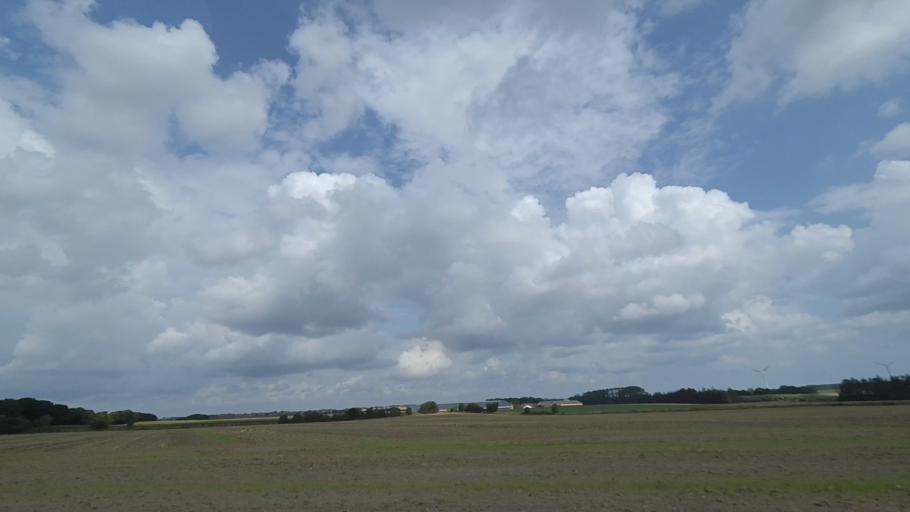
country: DK
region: Central Jutland
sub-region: Norddjurs Kommune
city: Allingabro
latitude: 56.5295
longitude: 10.3184
